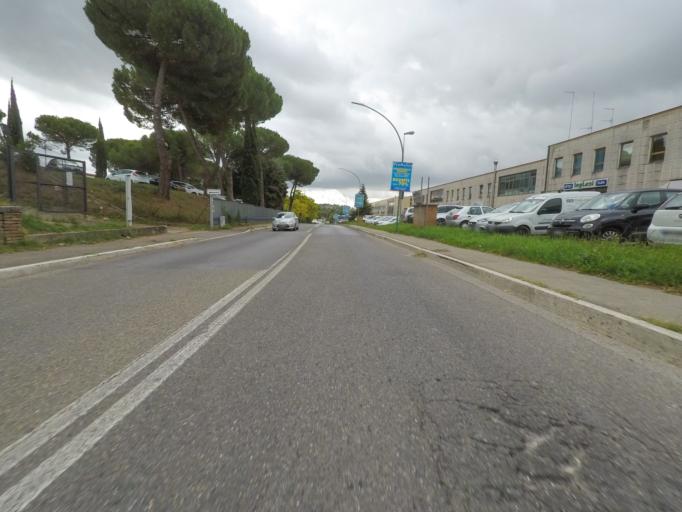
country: IT
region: Tuscany
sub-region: Provincia di Siena
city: Siena
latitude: 43.3193
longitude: 11.3512
